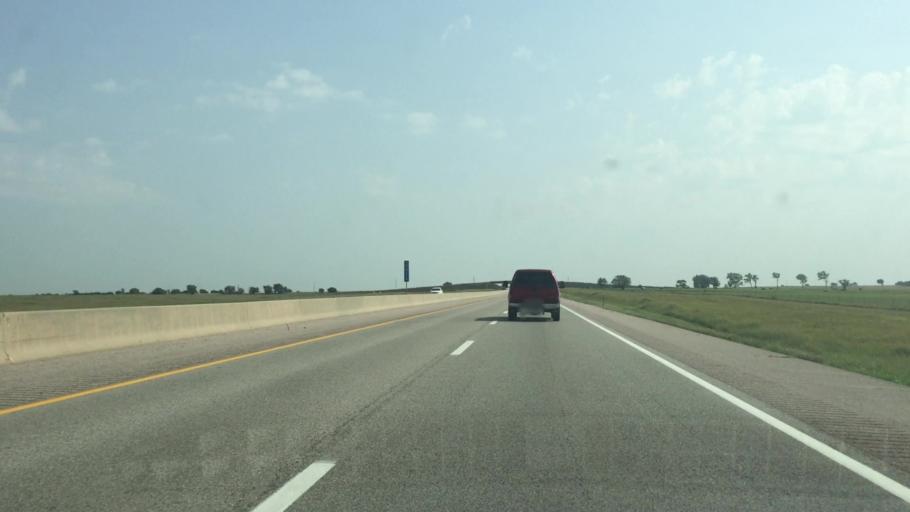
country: US
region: Kansas
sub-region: Butler County
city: El Dorado
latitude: 37.9930
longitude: -96.6984
